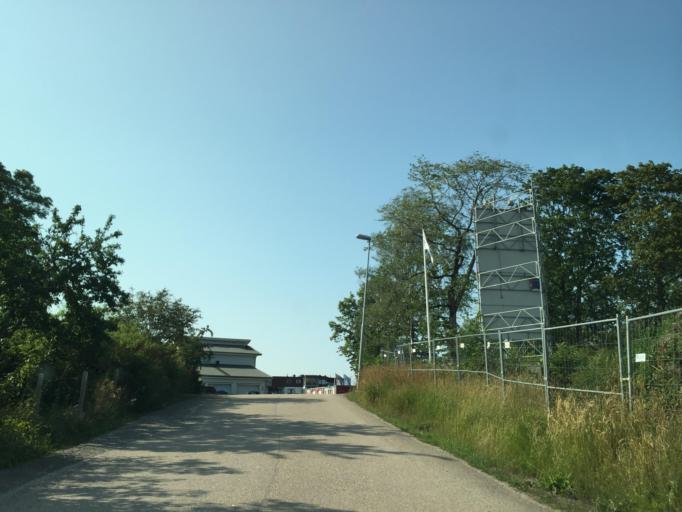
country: SE
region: Vaestra Goetaland
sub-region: Vanersborgs Kommun
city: Vanersborg
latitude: 58.3605
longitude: 12.3192
